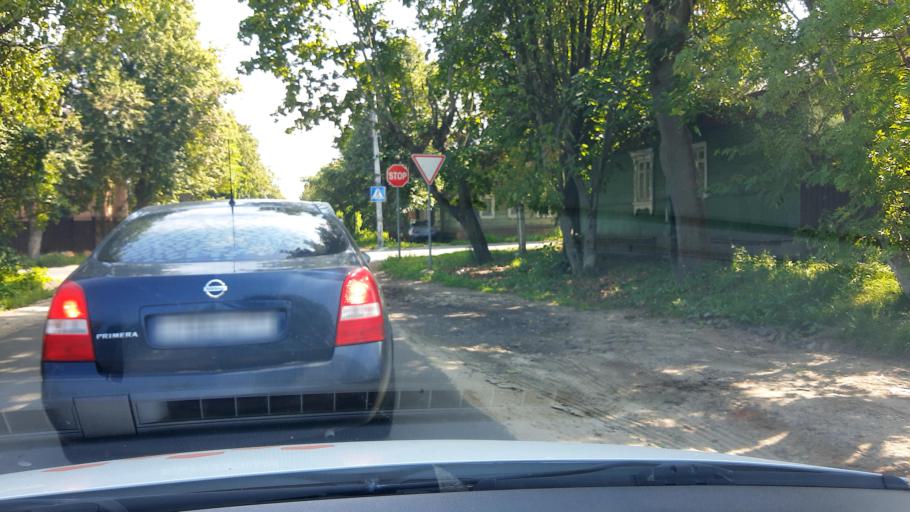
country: RU
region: Moskovskaya
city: Bronnitsy
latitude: 55.4237
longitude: 38.2610
